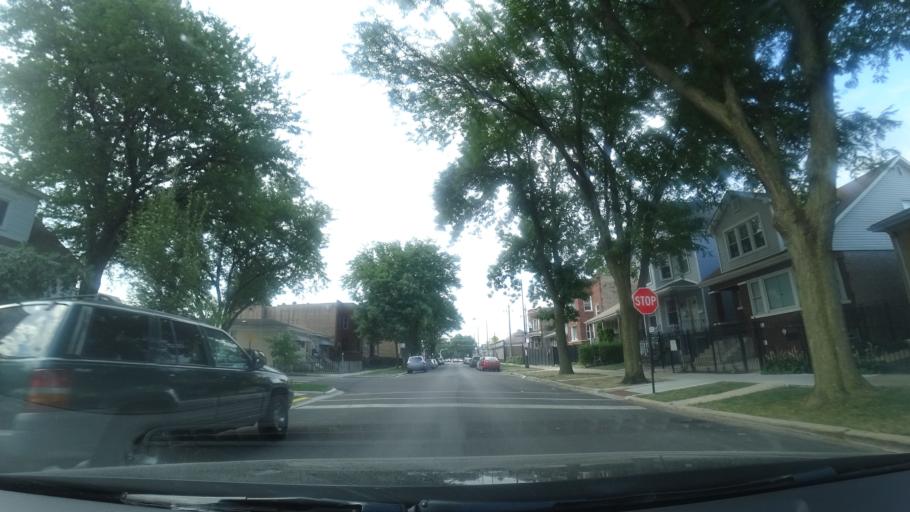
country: US
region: Illinois
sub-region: Cook County
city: Lincolnwood
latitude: 41.9402
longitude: -87.7370
